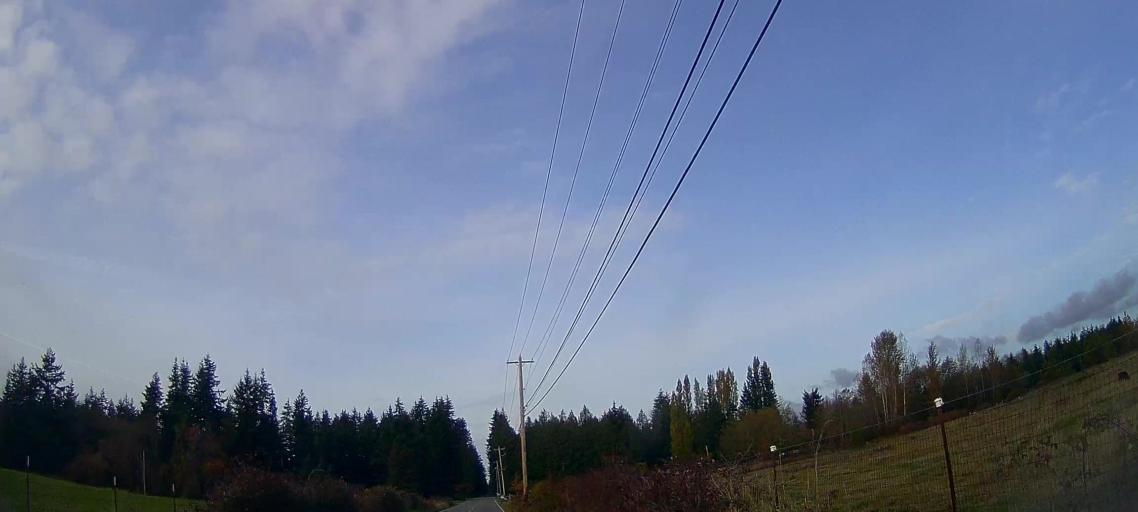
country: US
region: Washington
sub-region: Snohomish County
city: Stanwood
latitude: 48.2748
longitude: -122.3364
